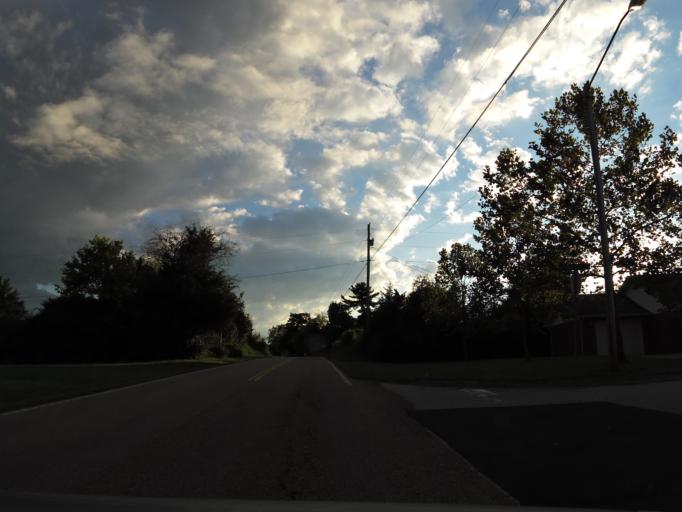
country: US
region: Tennessee
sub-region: Jefferson County
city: Jefferson City
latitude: 36.1170
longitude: -83.5087
